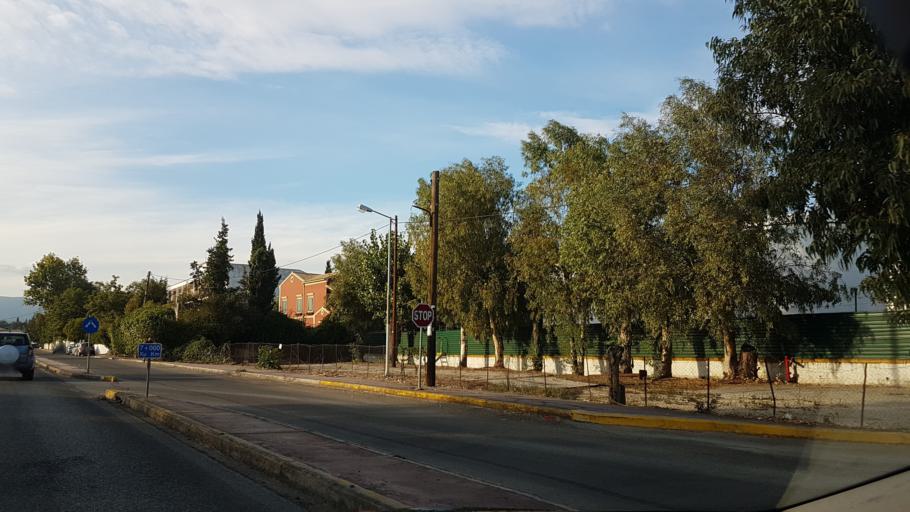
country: GR
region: Ionian Islands
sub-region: Nomos Kerkyras
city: Kontokali
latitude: 39.6497
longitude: 19.8448
